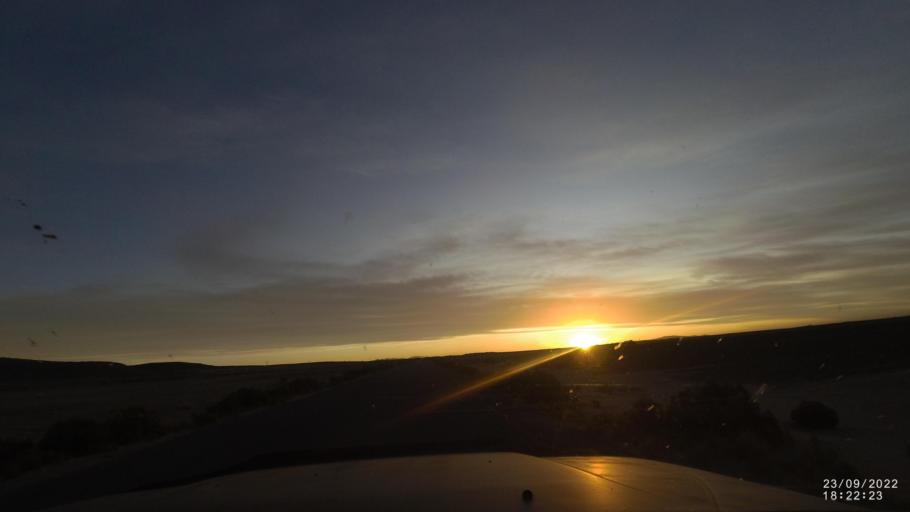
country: BO
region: Oruro
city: Challapata
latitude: -19.2880
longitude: -67.0850
